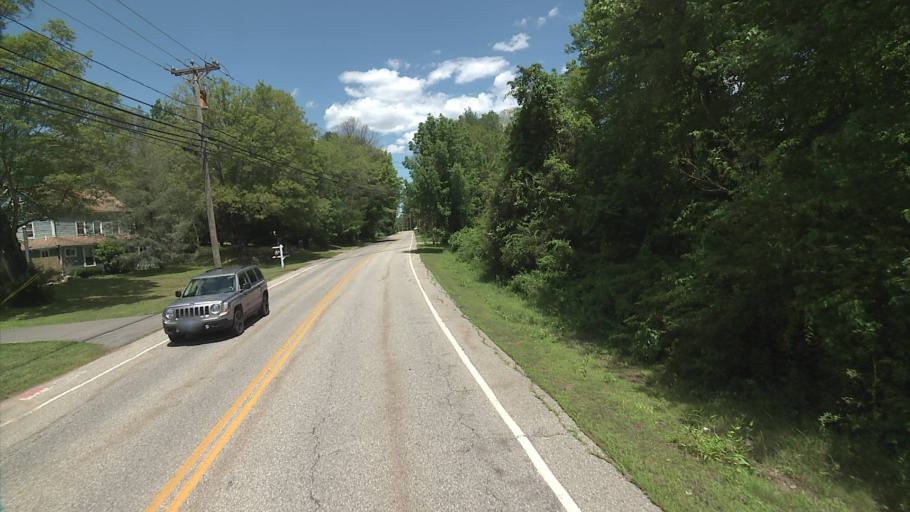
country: US
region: Connecticut
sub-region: Middlesex County
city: East Hampton
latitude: 41.5505
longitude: -72.5089
